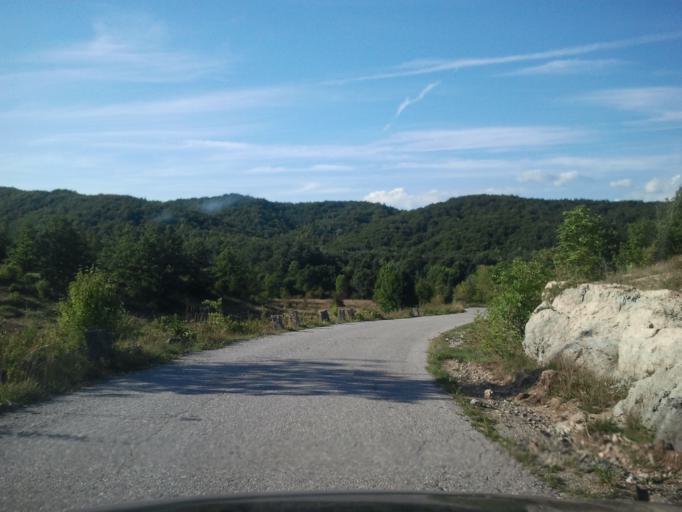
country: HR
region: Zadarska
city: Obrovac
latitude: 44.3308
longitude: 15.6396
